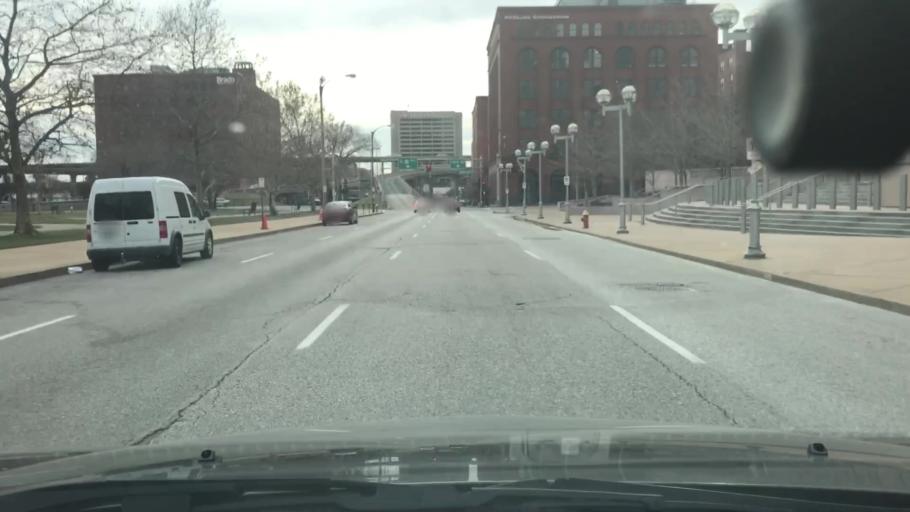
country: US
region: Missouri
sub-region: City of Saint Louis
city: St. Louis
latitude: 38.6255
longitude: -90.1961
